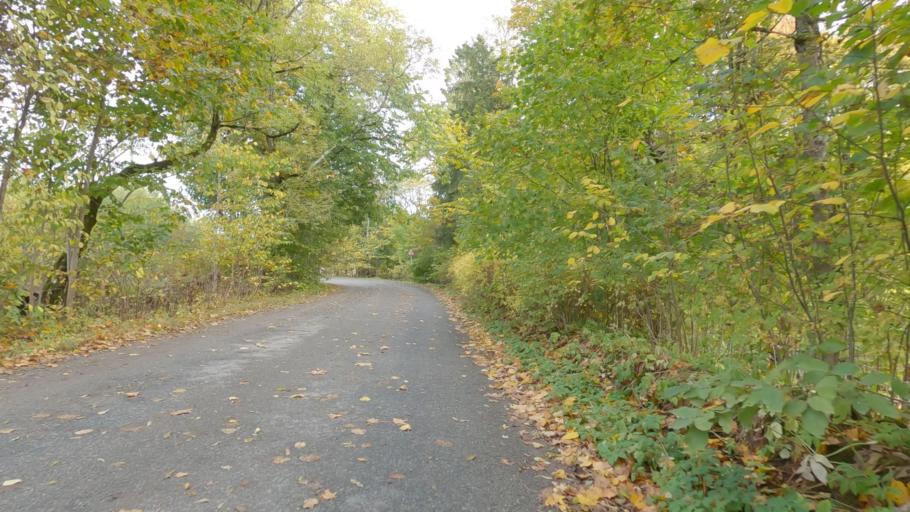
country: EE
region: Raplamaa
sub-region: Rapla vald
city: Rapla
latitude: 58.9356
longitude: 24.7585
